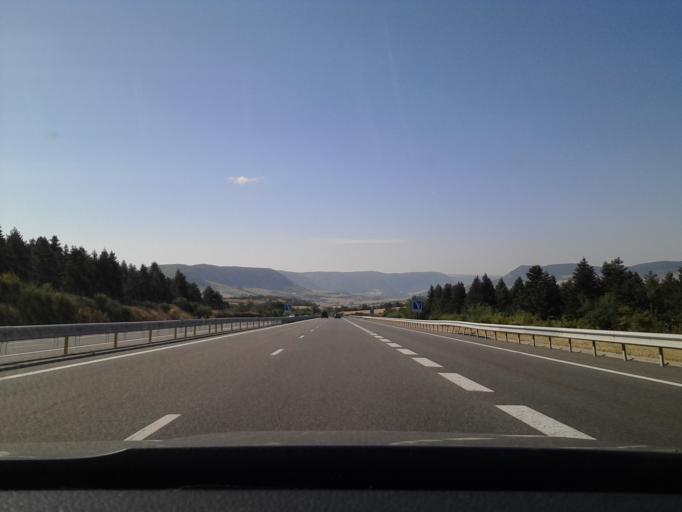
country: FR
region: Midi-Pyrenees
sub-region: Departement de l'Aveyron
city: Severac-le-Chateau
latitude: 44.2251
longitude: 3.0700
